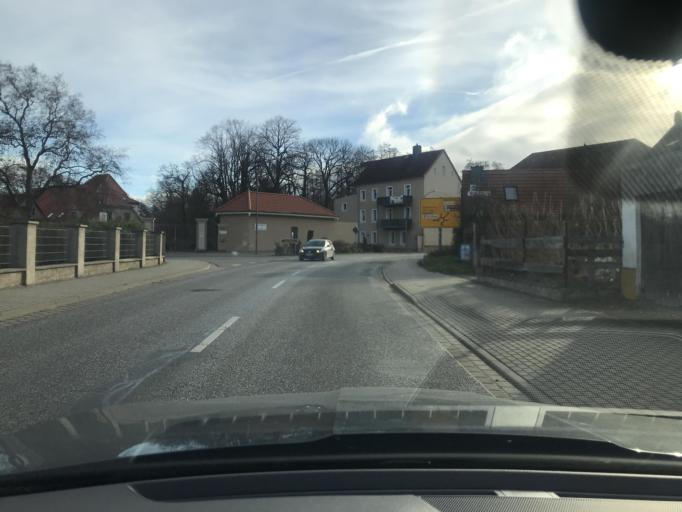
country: DE
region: Saxony-Anhalt
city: Thale
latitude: 51.7557
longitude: 11.0455
